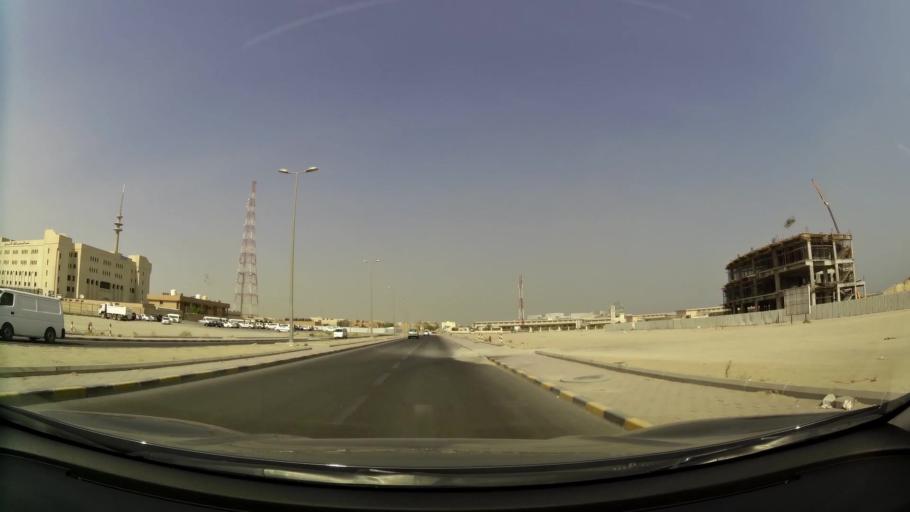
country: KW
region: Al Ahmadi
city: Al Fahahil
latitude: 29.0845
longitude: 48.1085
